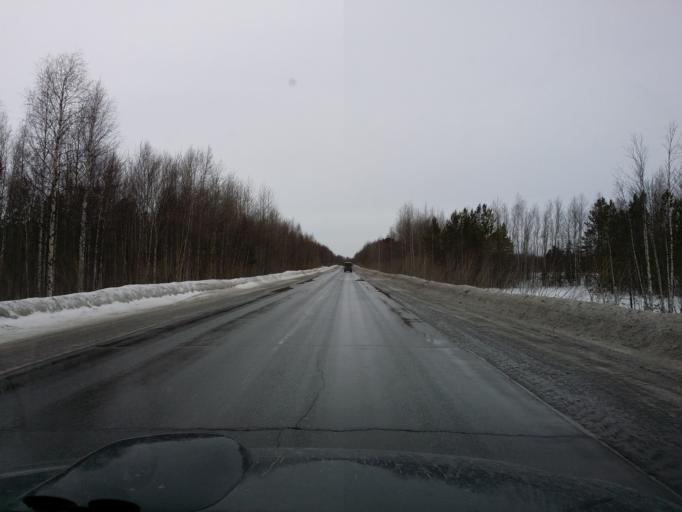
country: RU
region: Tomsk
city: Strezhevoy
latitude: 60.7432
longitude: 77.5274
